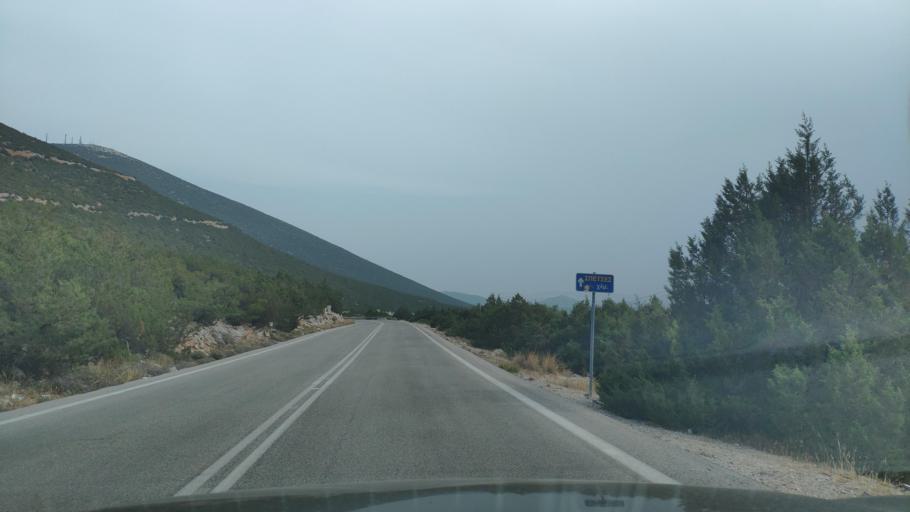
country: GR
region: Peloponnese
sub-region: Nomos Argolidos
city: Didyma
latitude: 37.4997
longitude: 23.1908
